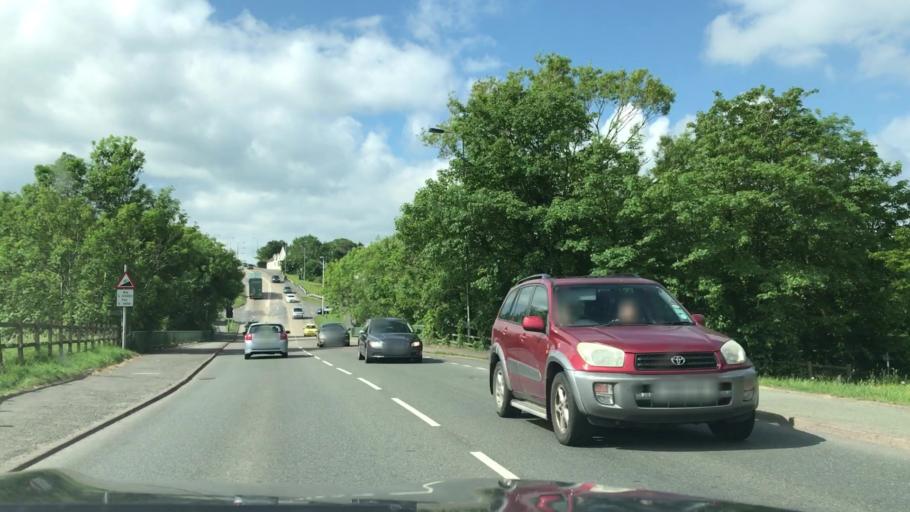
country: GB
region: Wales
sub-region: County of Ceredigion
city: Penparcau
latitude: 52.4033
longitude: -4.0669
